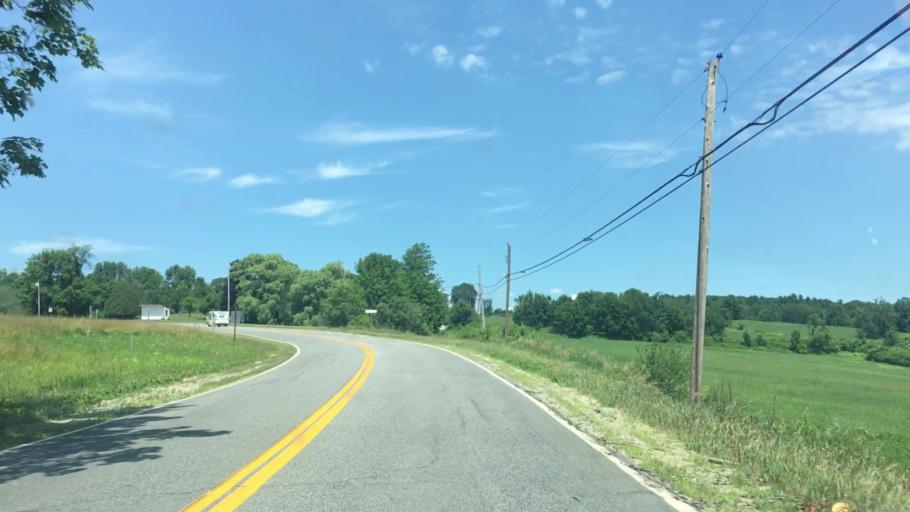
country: US
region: Maine
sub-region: Androscoggin County
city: Livermore
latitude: 44.3824
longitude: -70.2069
